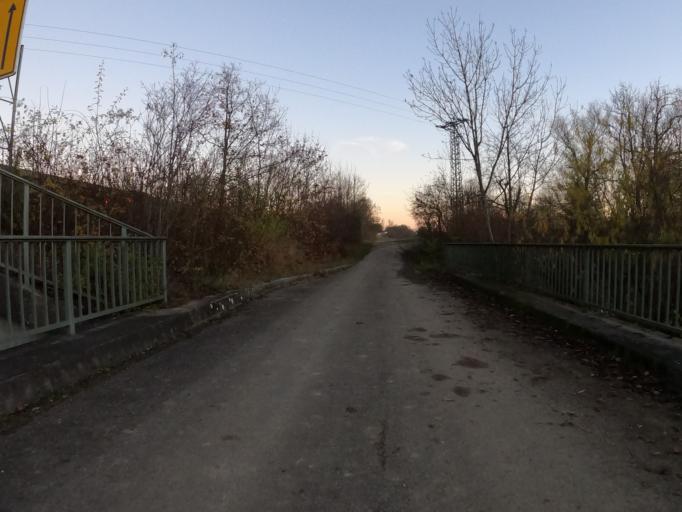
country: DE
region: Bavaria
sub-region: Swabia
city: Nersingen
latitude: 48.4300
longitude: 10.1054
